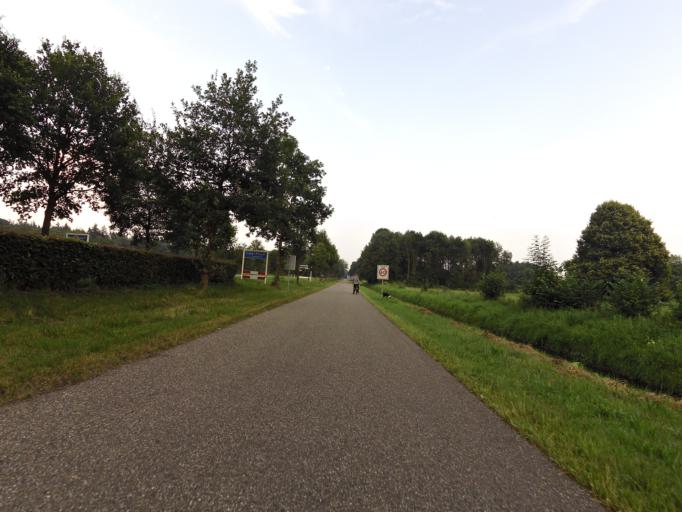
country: NL
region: Gelderland
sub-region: Gemeente Doetinchem
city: Doetinchem
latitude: 51.9956
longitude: 6.2277
